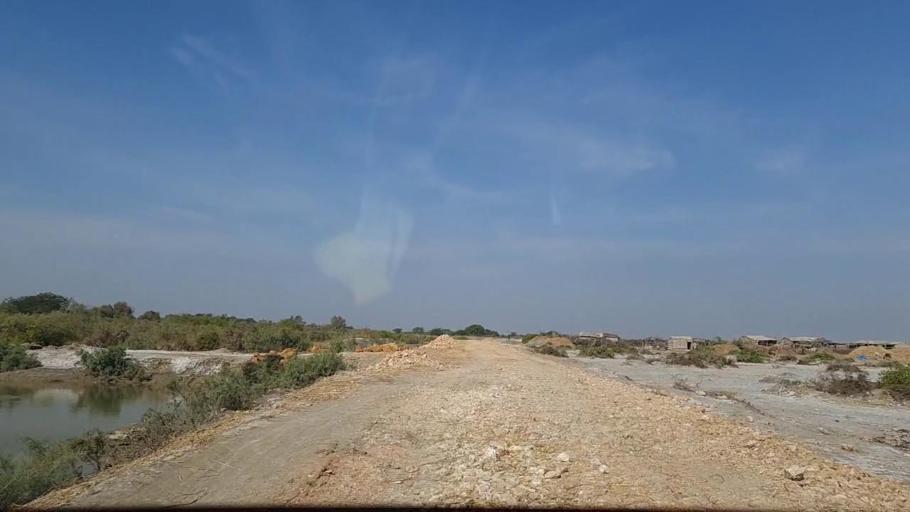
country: PK
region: Sindh
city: Daro Mehar
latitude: 24.7071
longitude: 68.1502
